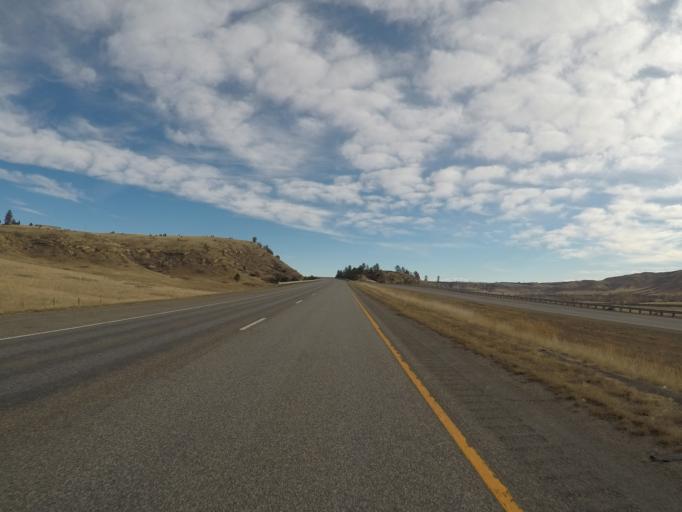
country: US
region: Montana
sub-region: Stillwater County
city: Columbus
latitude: 45.5958
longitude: -109.0957
